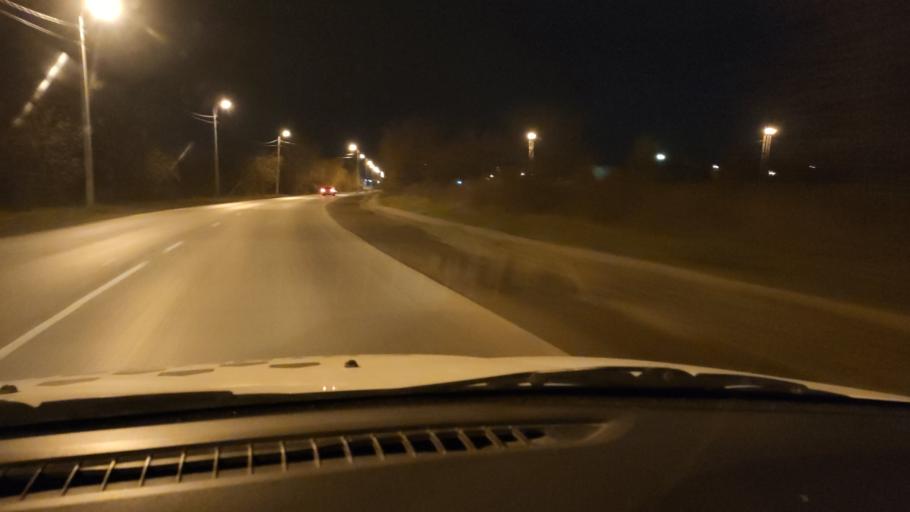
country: RU
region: Perm
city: Kondratovo
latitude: 57.9465
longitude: 56.1459
